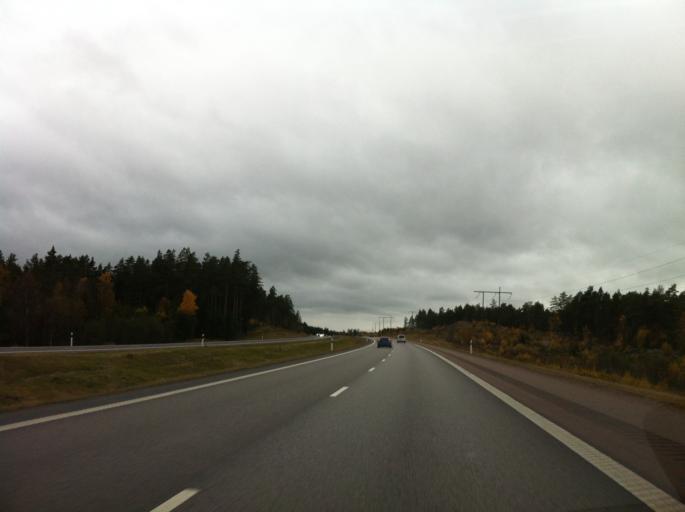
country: SE
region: OEstergoetland
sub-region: Vadstena Kommun
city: Herrestad
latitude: 58.2622
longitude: 14.8394
